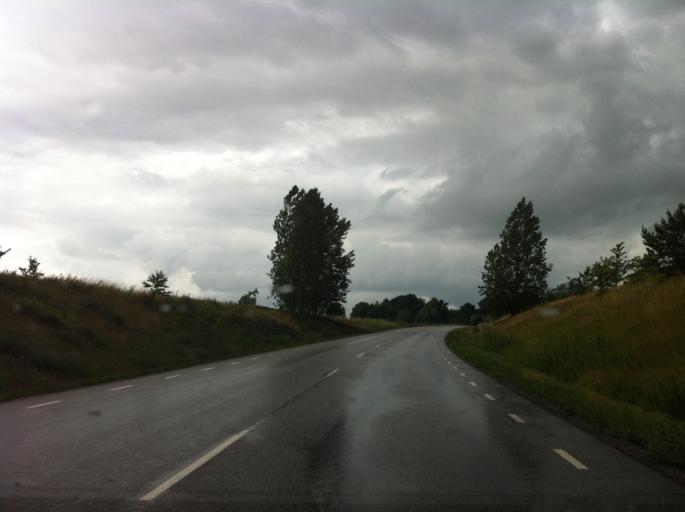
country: SE
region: Skane
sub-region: Lunds Kommun
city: Lund
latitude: 55.7914
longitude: 13.2201
